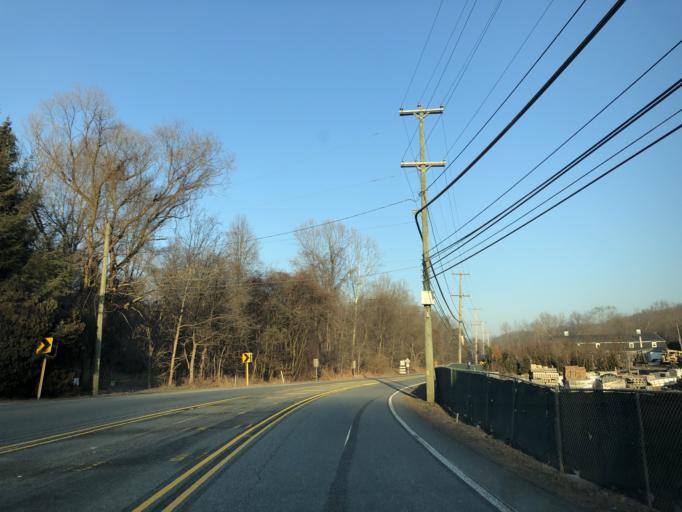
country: US
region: Pennsylvania
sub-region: Chester County
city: Downingtown
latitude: 39.9686
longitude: -75.6754
